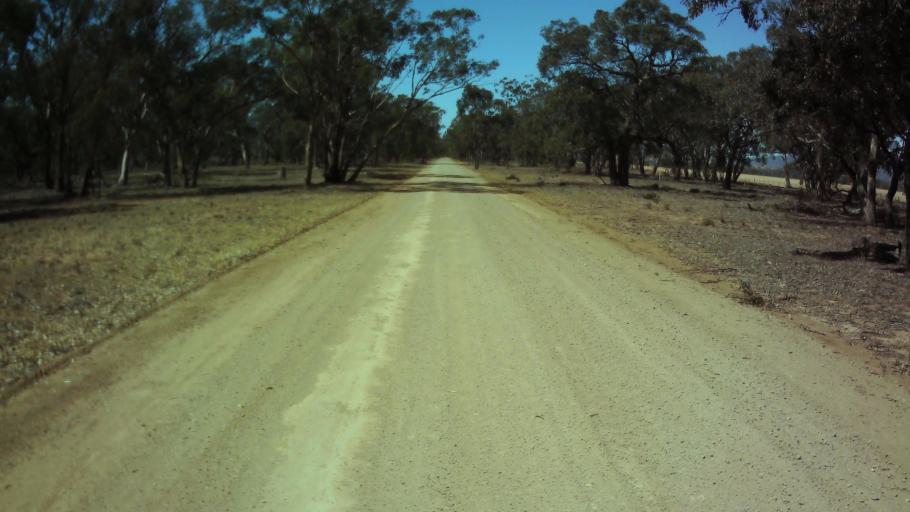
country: AU
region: New South Wales
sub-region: Weddin
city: Grenfell
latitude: -33.8508
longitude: 148.0883
